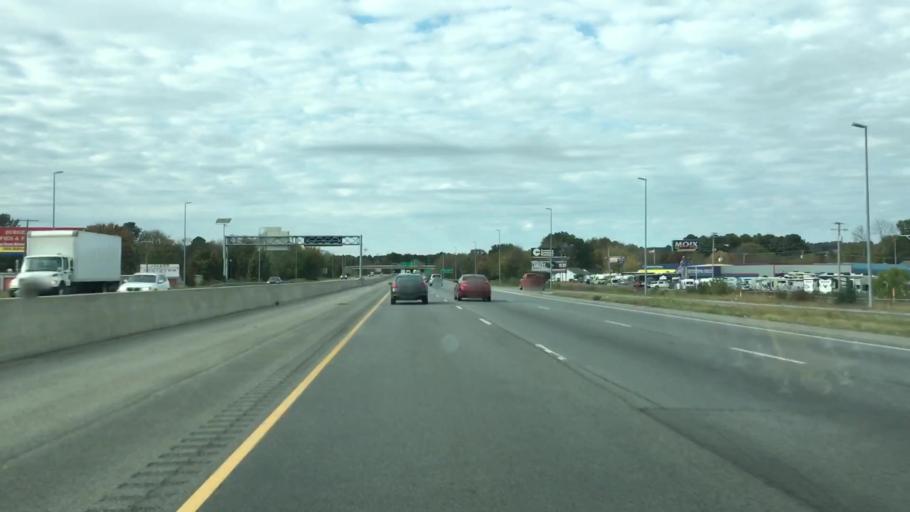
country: US
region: Arkansas
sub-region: Faulkner County
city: Conway
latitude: 35.0945
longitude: -92.4255
